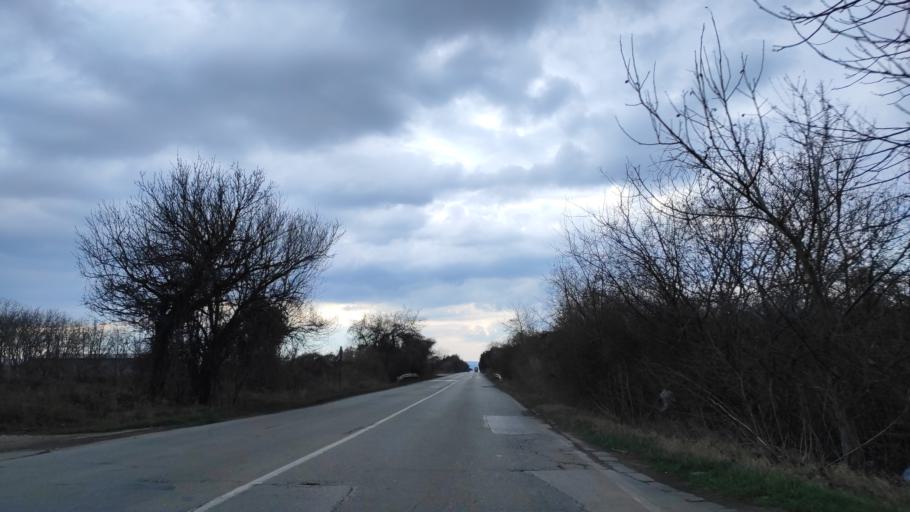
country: BG
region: Varna
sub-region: Obshtina Aksakovo
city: Aksakovo
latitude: 43.2294
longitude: 27.8226
